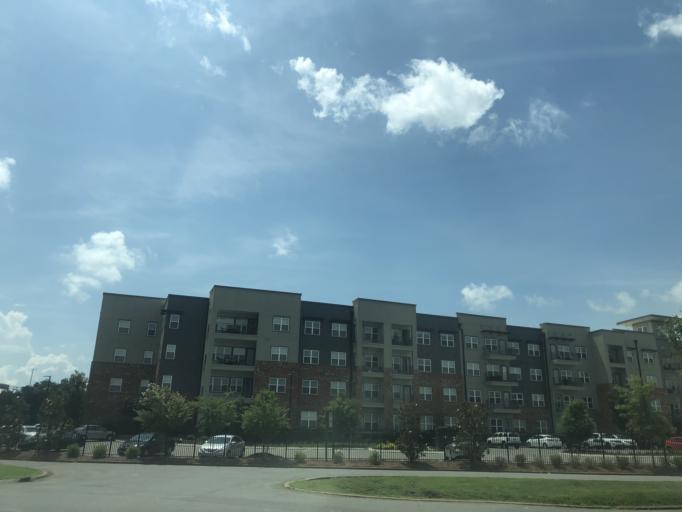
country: US
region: Tennessee
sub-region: Davidson County
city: Nashville
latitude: 36.1937
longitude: -86.7898
